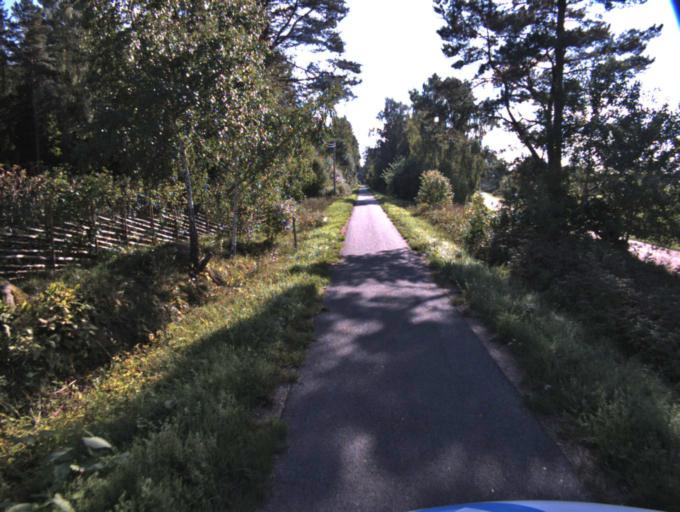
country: SE
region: Vaestra Goetaland
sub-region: Boras Kommun
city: Dalsjofors
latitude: 57.8202
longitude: 13.1527
